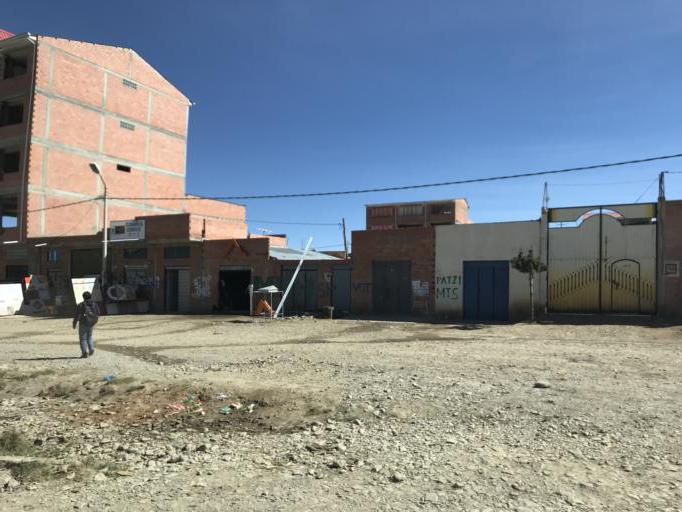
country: BO
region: La Paz
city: La Paz
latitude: -16.5040
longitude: -68.2492
